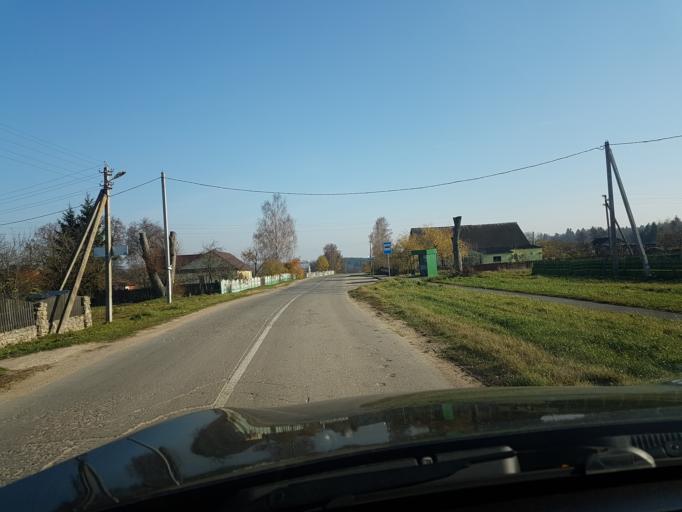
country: BY
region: Minsk
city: Azyartso
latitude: 53.8182
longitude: 27.3600
